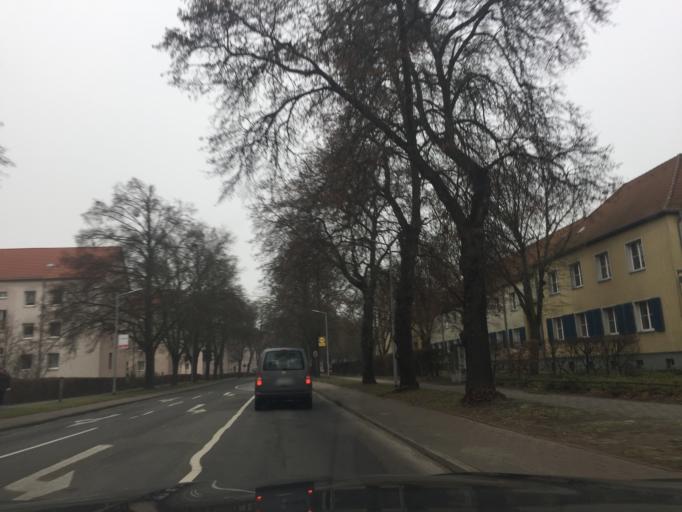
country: DE
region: Brandenburg
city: Hennigsdorf
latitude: 52.6475
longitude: 13.2013
